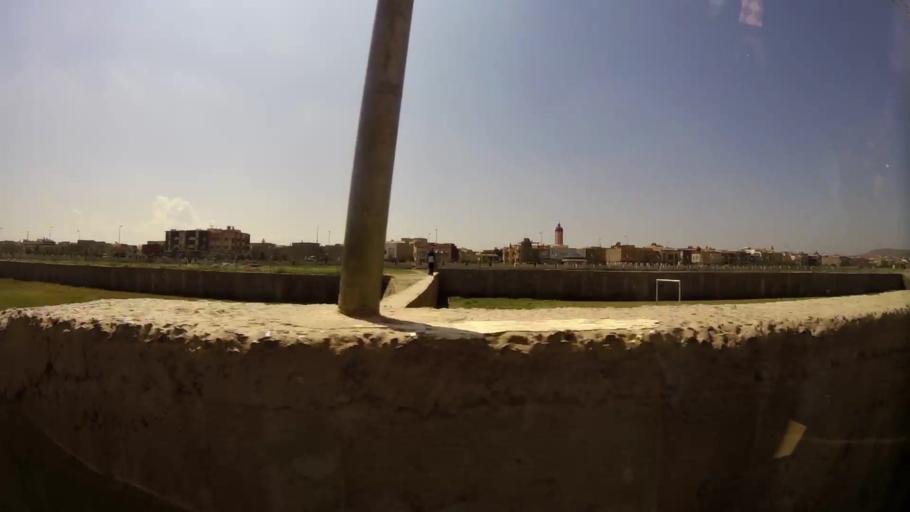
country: MA
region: Oriental
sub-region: Oujda-Angad
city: Oujda
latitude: 34.6680
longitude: -1.9419
